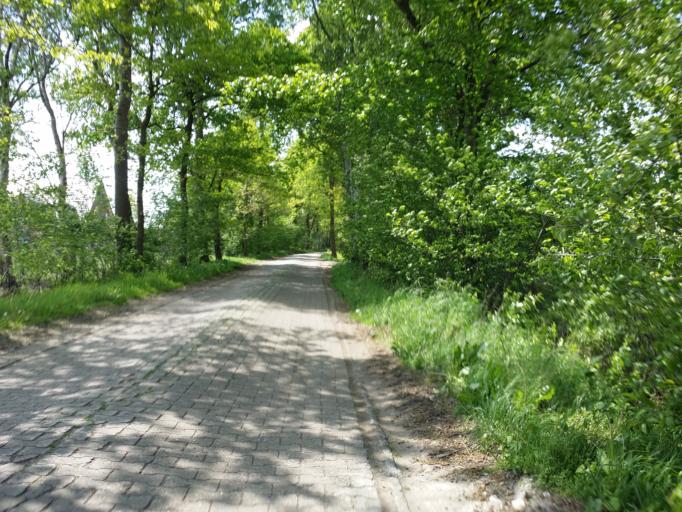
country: DE
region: Lower Saxony
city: Axstedt
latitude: 53.2986
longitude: 8.7357
